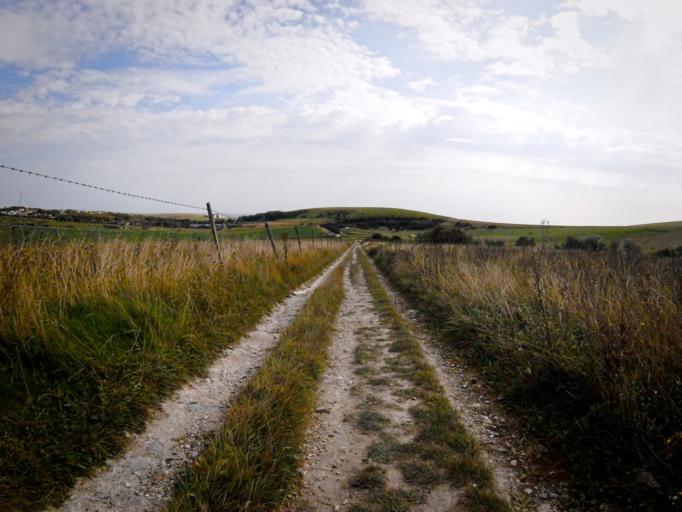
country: GB
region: England
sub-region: Brighton and Hove
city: Rottingdean
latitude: 50.8234
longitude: -0.0850
